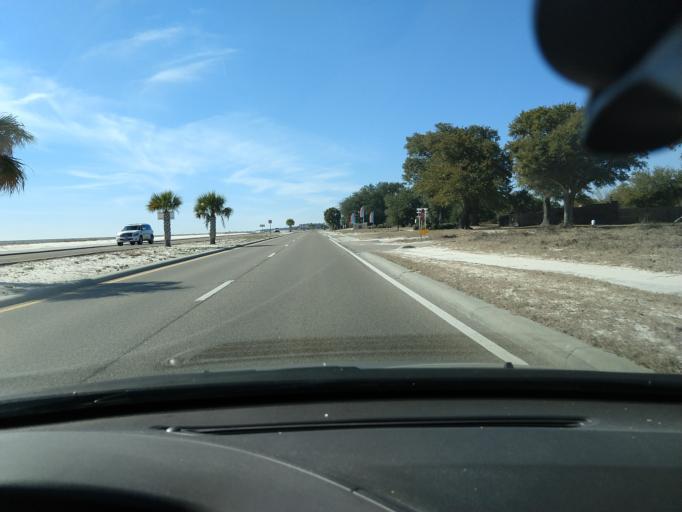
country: US
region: Mississippi
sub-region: Harrison County
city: Long Beach
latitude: 30.3324
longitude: -89.1847
